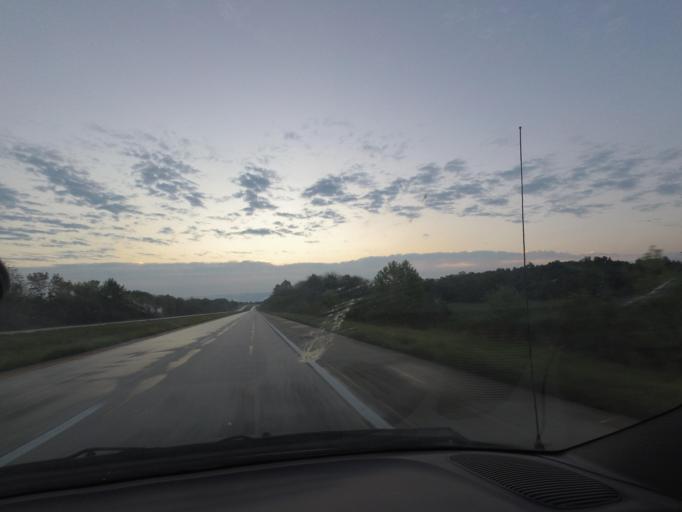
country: US
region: Missouri
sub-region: Macon County
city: Macon
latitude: 39.7592
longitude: -92.5938
